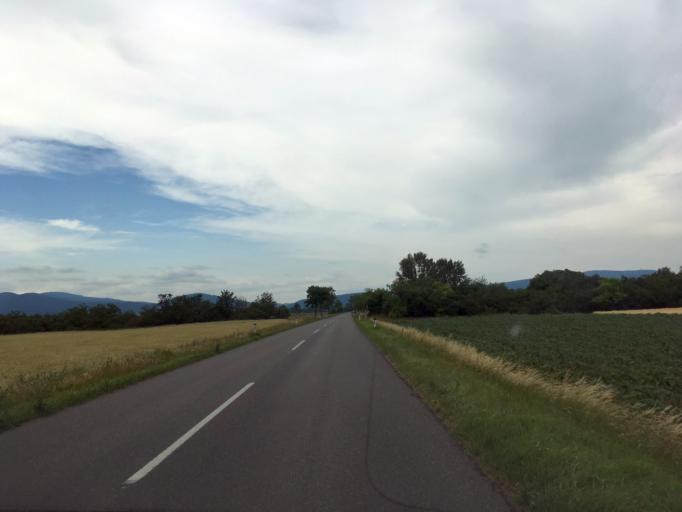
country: AT
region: Lower Austria
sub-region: Politischer Bezirk Baden
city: Teesdorf
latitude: 47.9567
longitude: 16.2751
